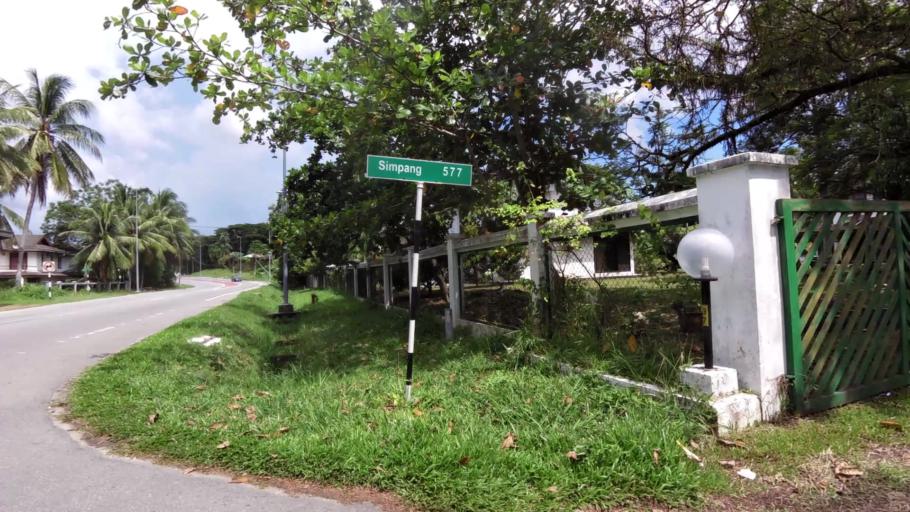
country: BN
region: Brunei and Muara
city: Bandar Seri Begawan
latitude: 4.9907
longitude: 114.9503
